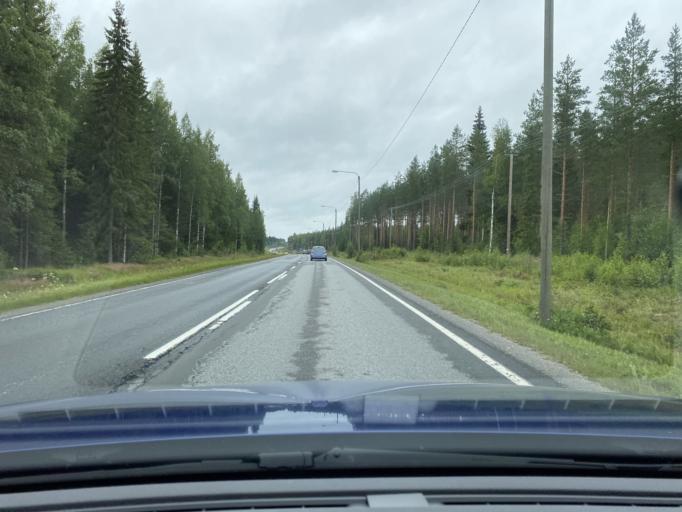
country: FI
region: Central Finland
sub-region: Keuruu
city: Keuruu
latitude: 62.2390
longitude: 24.4908
